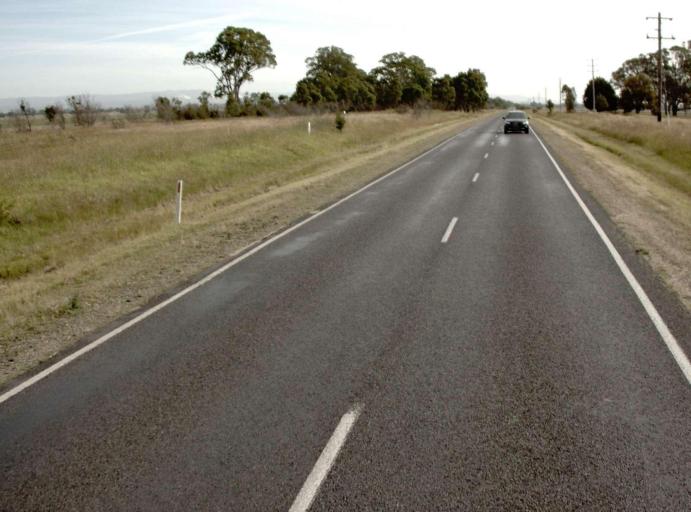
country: AU
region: Victoria
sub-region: Latrobe
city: Traralgon
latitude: -38.0755
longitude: 146.6116
